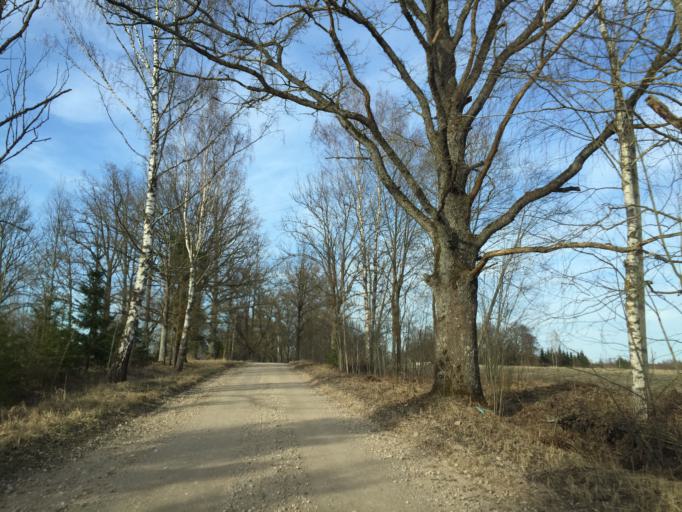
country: LV
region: Kegums
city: Kegums
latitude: 56.8057
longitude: 24.7779
